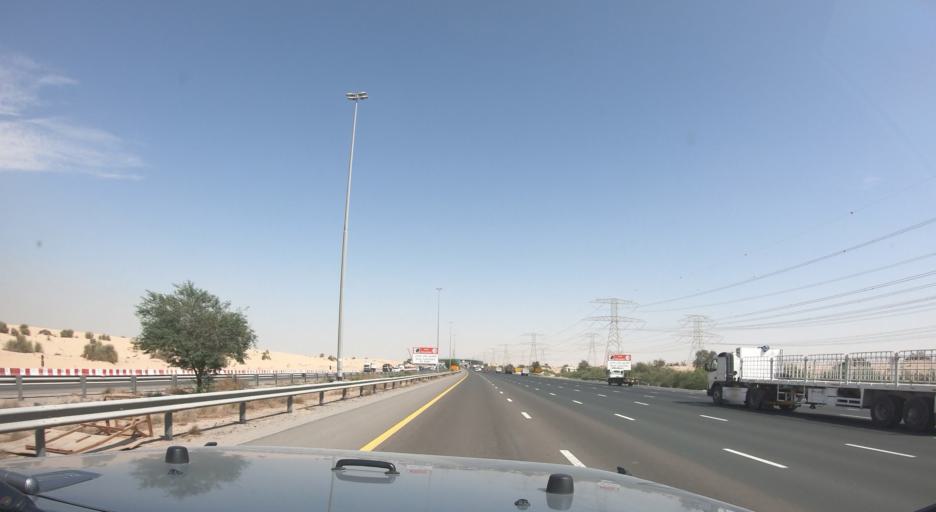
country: AE
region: Ash Shariqah
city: Sharjah
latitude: 25.1737
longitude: 55.5096
